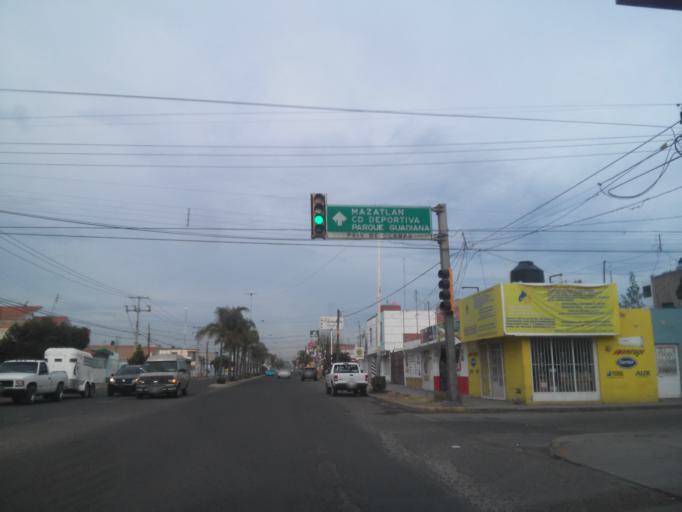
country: MX
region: Durango
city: Victoria de Durango
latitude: 24.0095
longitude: -104.6656
